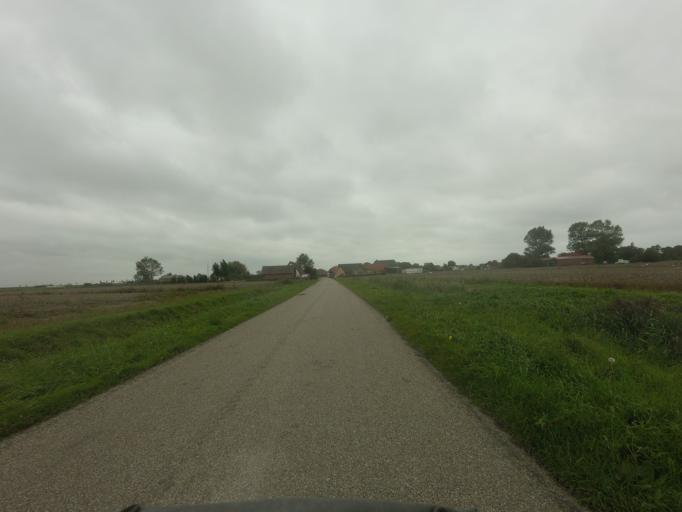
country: NL
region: Friesland
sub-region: Gemeente Dongeradeel
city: Holwerd
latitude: 53.3539
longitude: 5.8683
